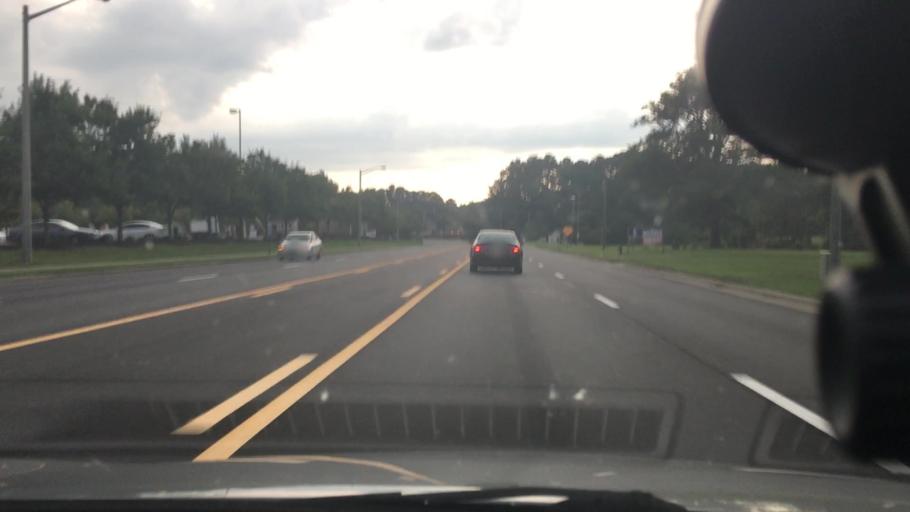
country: US
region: North Carolina
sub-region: Pitt County
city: Greenville
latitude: 35.5899
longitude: -77.3172
